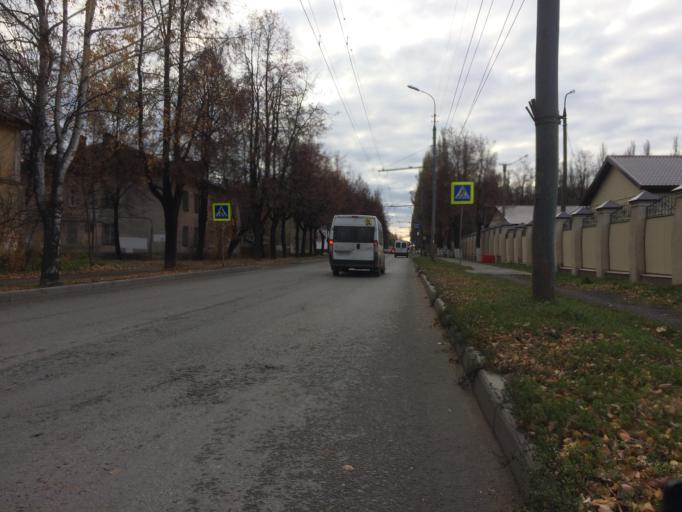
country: RU
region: Mariy-El
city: Yoshkar-Ola
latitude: 56.6386
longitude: 47.8615
